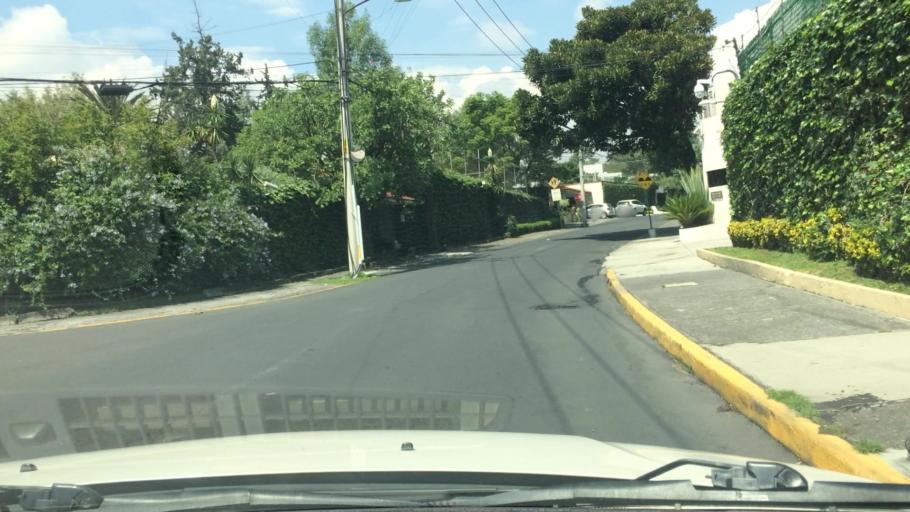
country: MX
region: Mexico City
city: Magdalena Contreras
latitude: 19.3263
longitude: -99.2090
